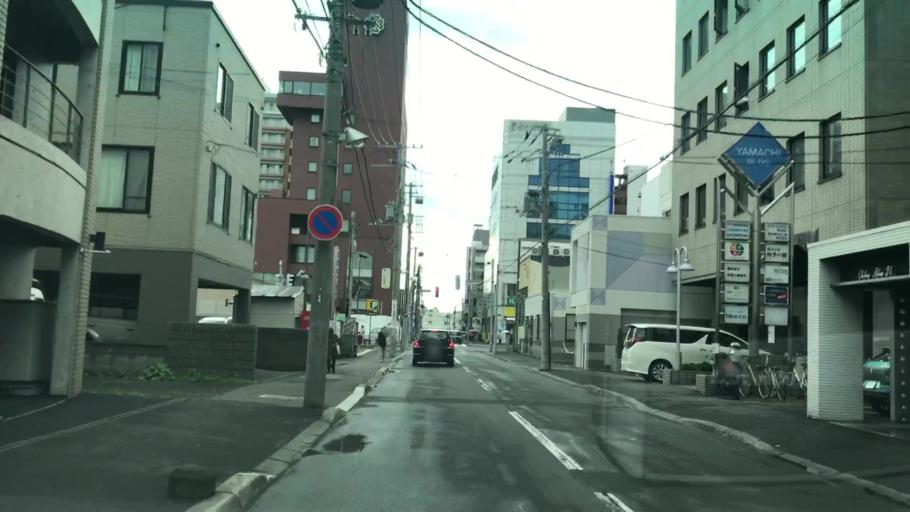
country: JP
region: Hokkaido
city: Sapporo
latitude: 43.0776
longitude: 141.3035
